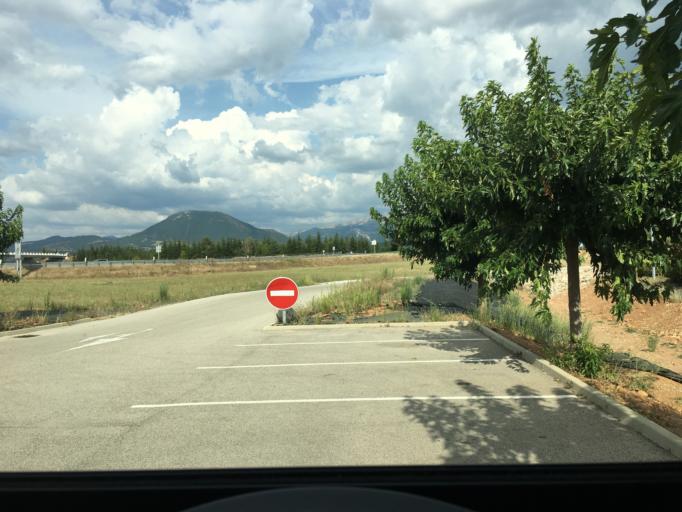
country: FR
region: Provence-Alpes-Cote d'Azur
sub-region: Departement des Alpes-de-Haute-Provence
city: Sisteron
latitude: 44.2371
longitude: 5.9113
